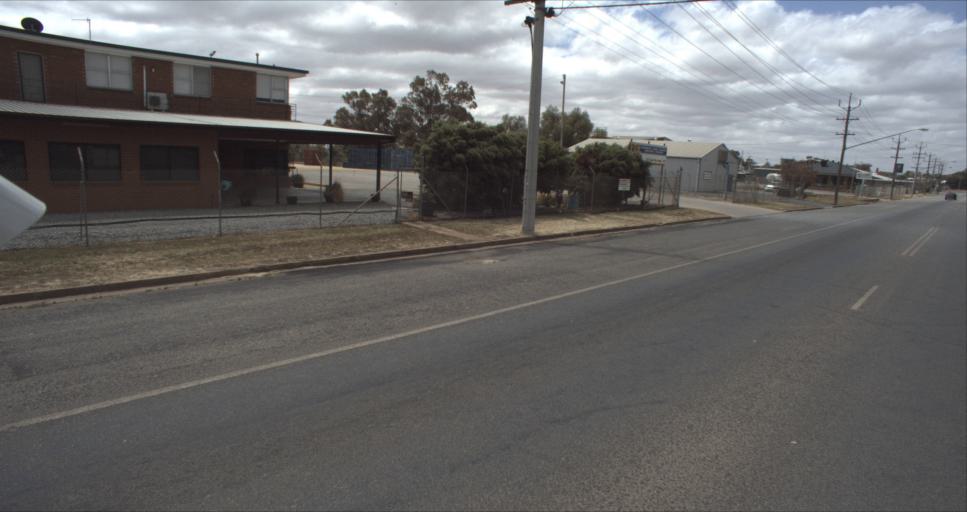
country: AU
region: New South Wales
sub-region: Leeton
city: Leeton
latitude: -34.5535
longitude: 146.3906
